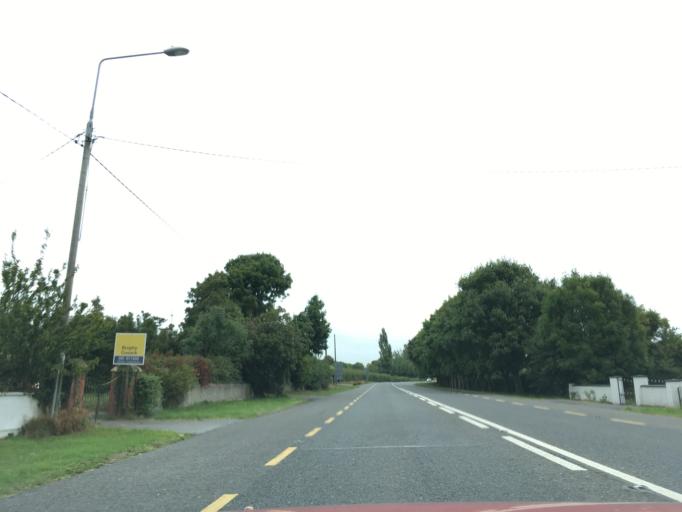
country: IE
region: Munster
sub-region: South Tipperary
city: Cluain Meala
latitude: 52.3623
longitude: -7.5694
